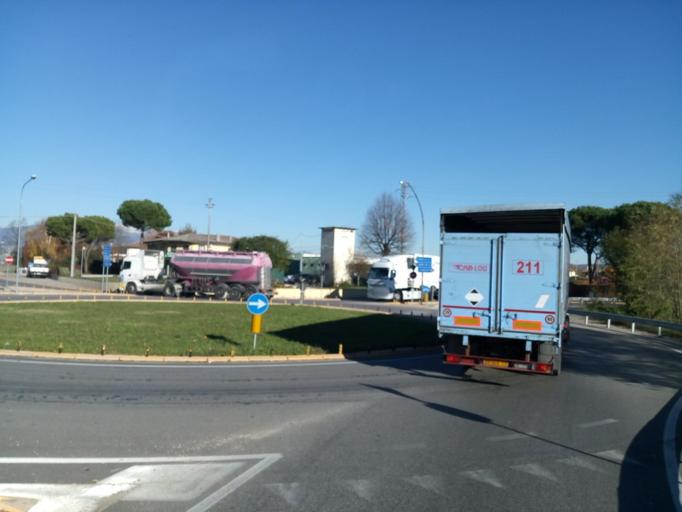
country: IT
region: Veneto
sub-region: Provincia di Treviso
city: Caerano di San Marco
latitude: 45.7631
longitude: 11.9950
